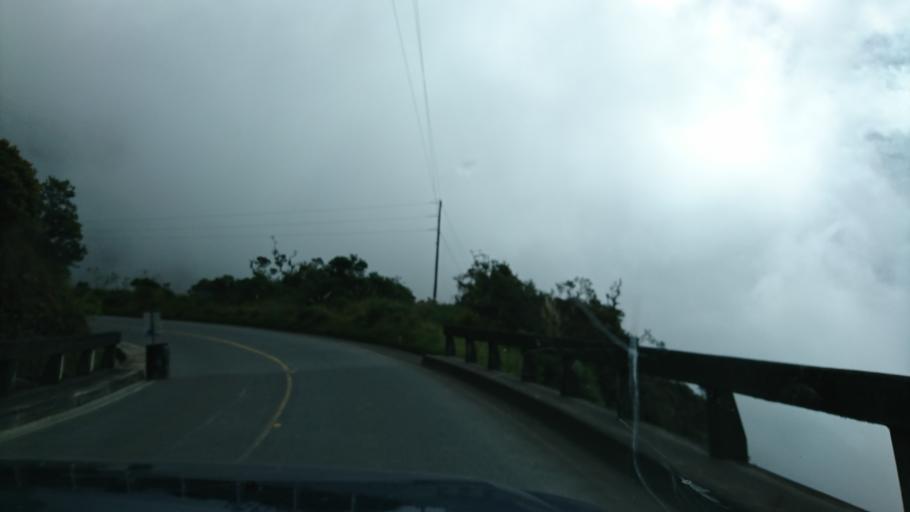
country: BO
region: La Paz
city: Coroico
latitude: -16.2703
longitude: -67.8264
